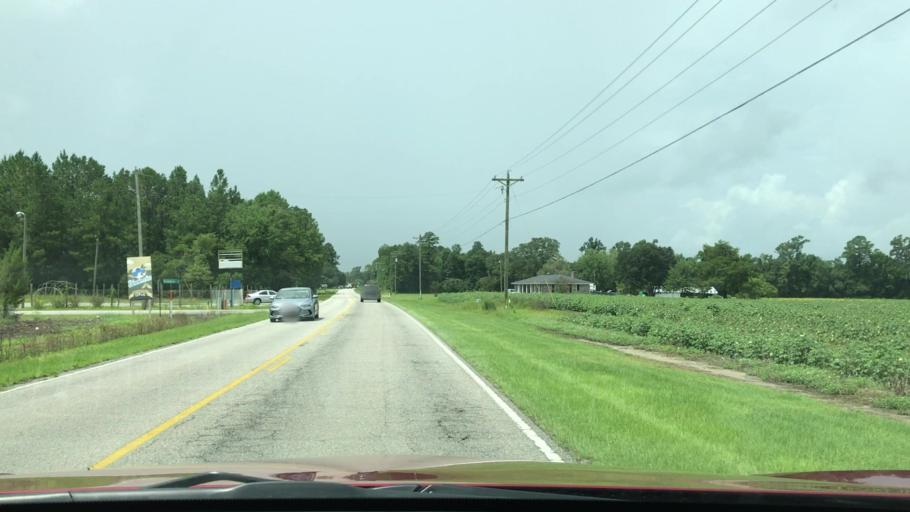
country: US
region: South Carolina
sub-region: Horry County
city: Red Hill
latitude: 33.8923
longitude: -78.9474
